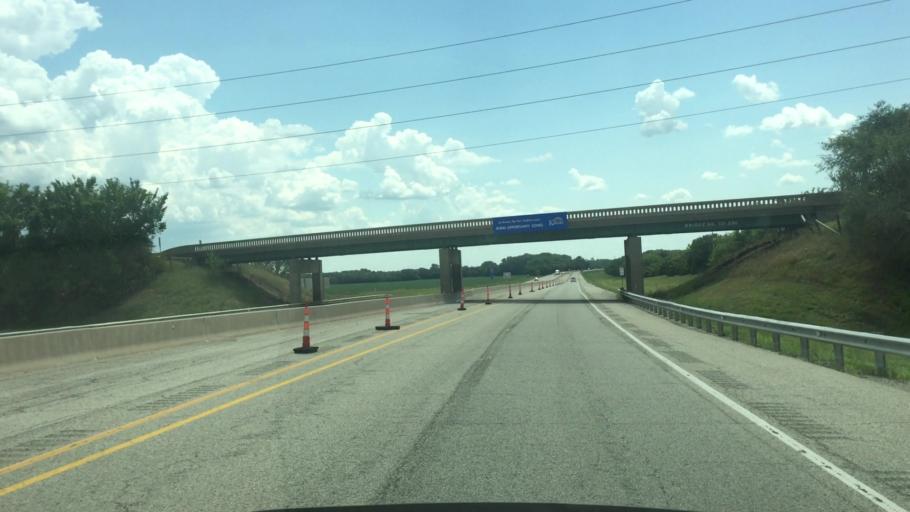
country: US
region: Kansas
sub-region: Lyon County
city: Emporia
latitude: 38.4649
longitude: -96.1898
